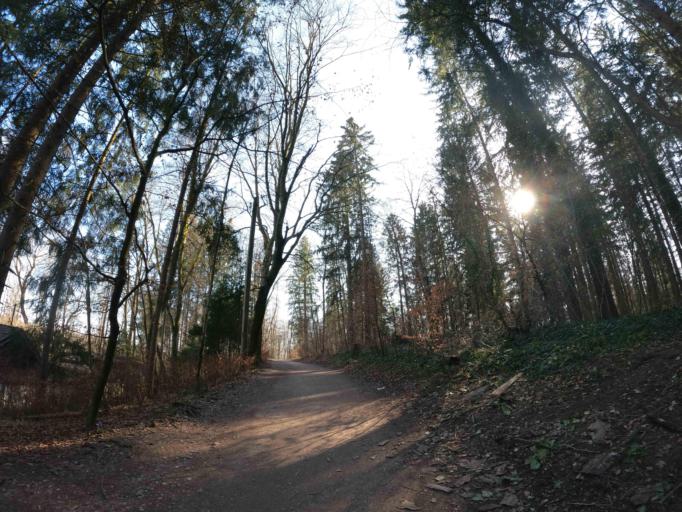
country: DE
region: Bavaria
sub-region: Upper Bavaria
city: Pullach im Isartal
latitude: 48.0663
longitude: 11.5383
